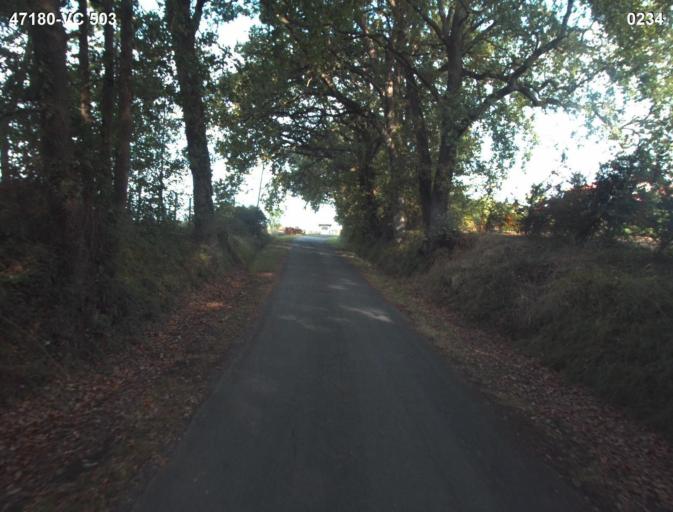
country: FR
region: Aquitaine
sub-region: Departement du Lot-et-Garonne
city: Port-Sainte-Marie
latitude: 44.1813
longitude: 0.4296
